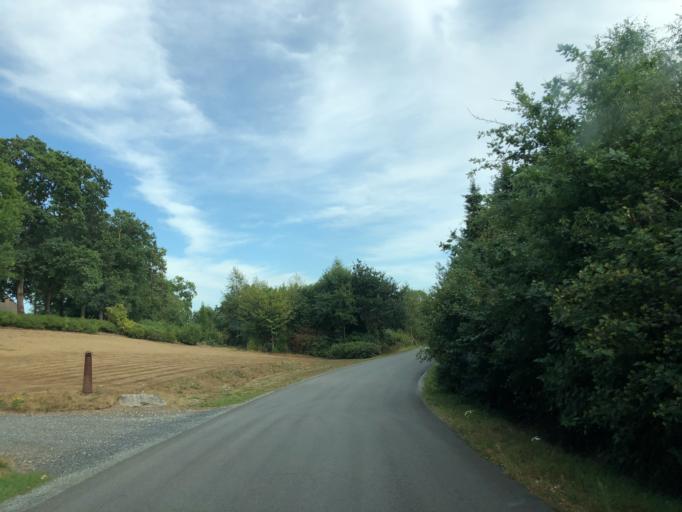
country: DK
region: South Denmark
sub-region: Vejle Kommune
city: Egtved
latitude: 55.6810
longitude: 9.2670
